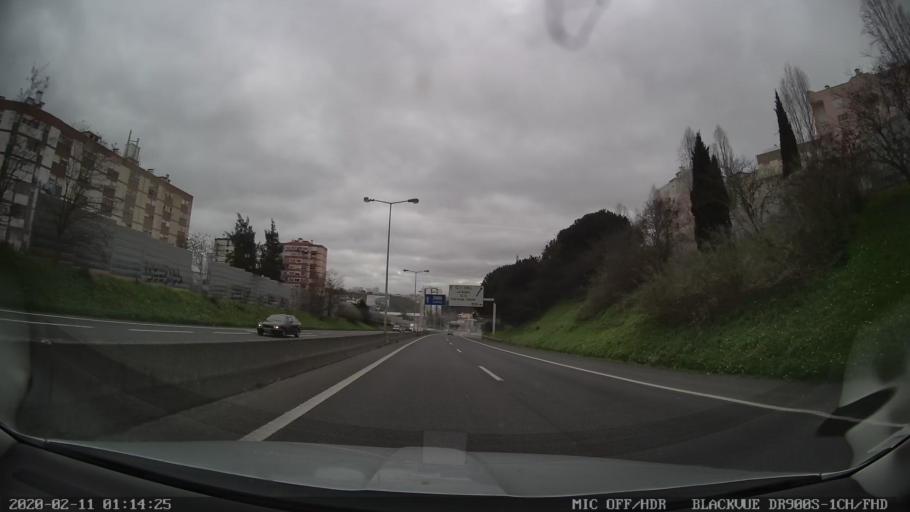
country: PT
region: Lisbon
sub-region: Odivelas
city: Povoa de Santo Adriao
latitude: 38.7980
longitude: -9.1748
